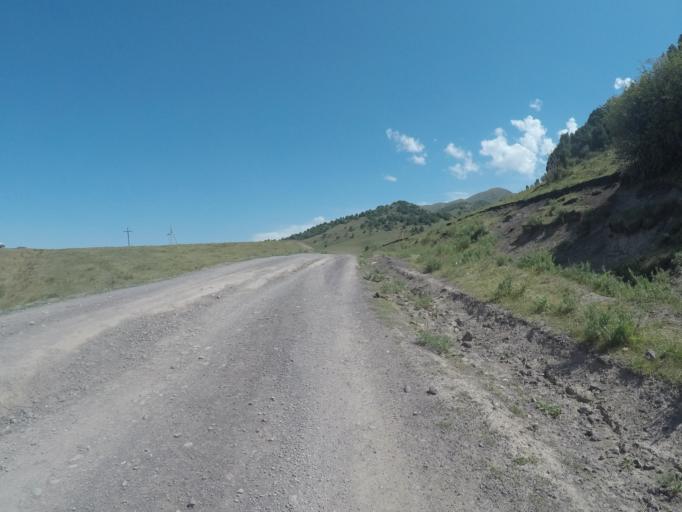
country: KG
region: Chuy
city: Bishkek
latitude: 42.6505
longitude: 74.5289
